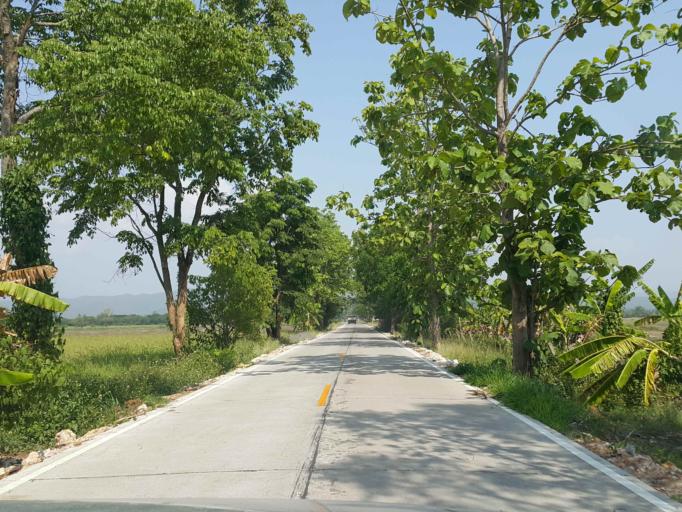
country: TH
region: Chiang Mai
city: San Kamphaeng
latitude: 18.7920
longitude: 99.1501
